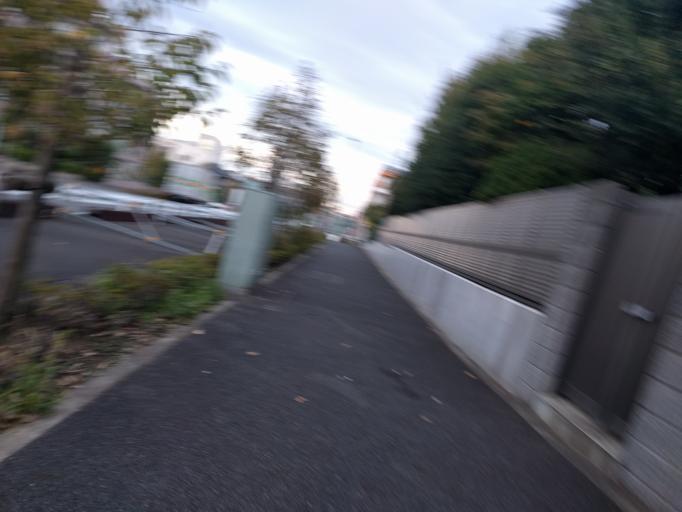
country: JP
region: Tokyo
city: Tokyo
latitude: 35.6416
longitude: 139.6426
